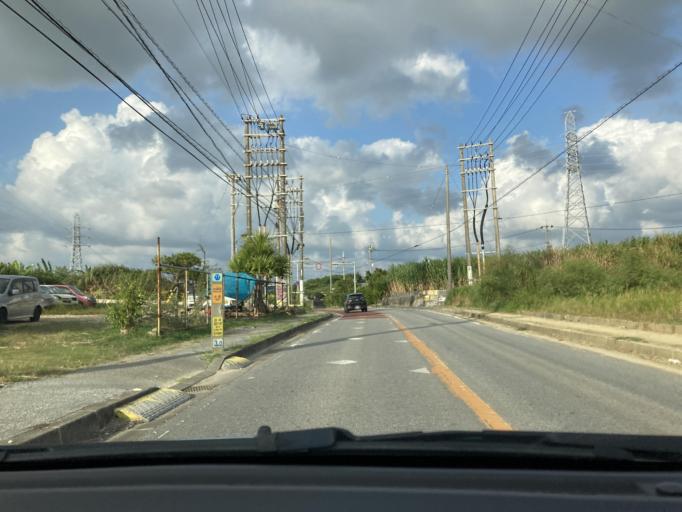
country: JP
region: Okinawa
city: Itoman
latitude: 26.1347
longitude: 127.6921
